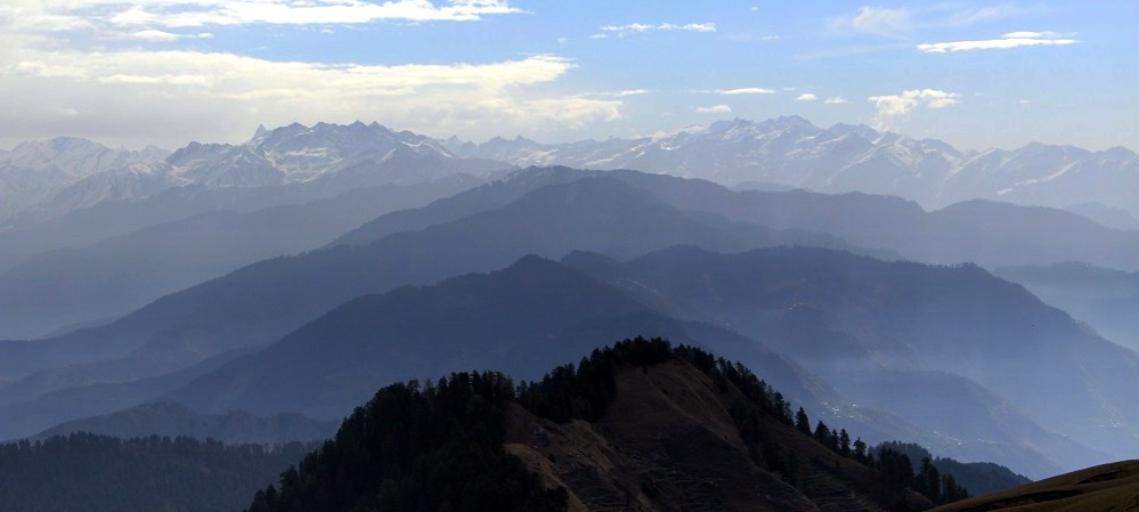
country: IN
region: Himachal Pradesh
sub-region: Mandi
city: Pandoh
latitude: 31.7484
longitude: 77.1162
